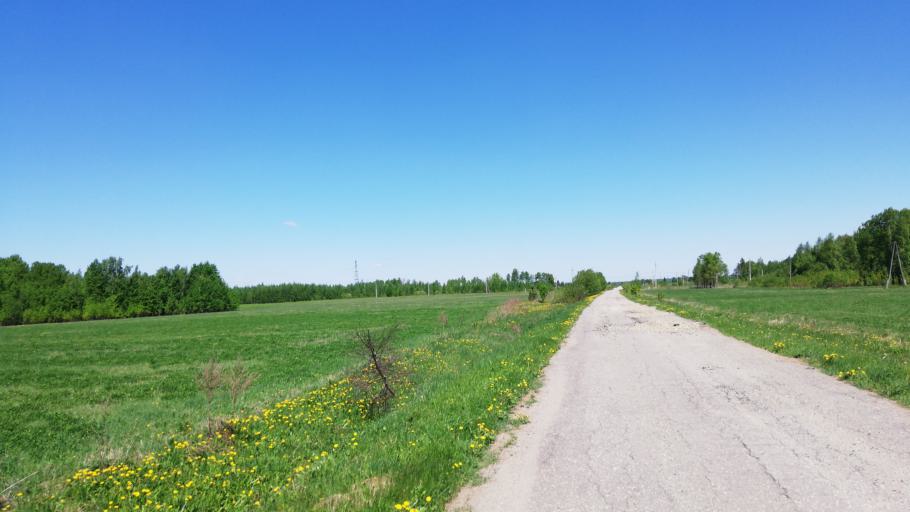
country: RU
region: Ivanovo
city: Pistsovo
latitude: 57.1208
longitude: 40.5986
